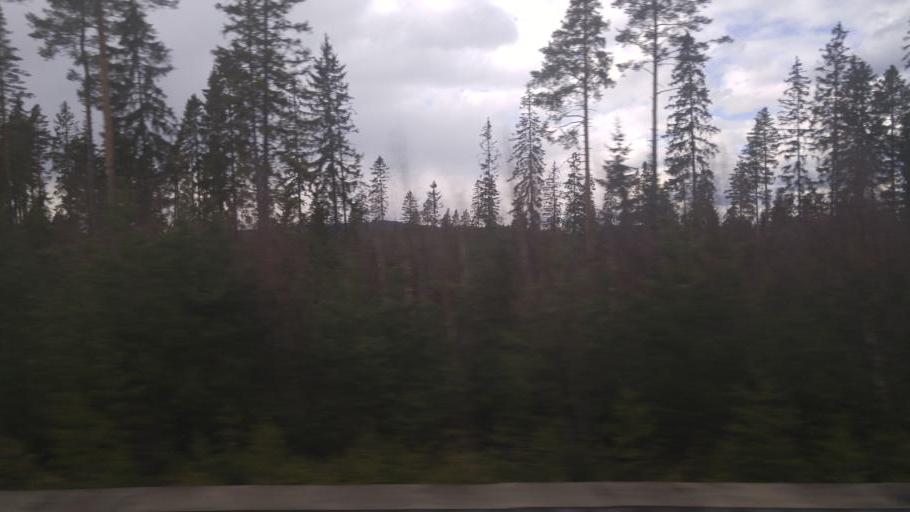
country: NO
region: Akershus
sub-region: Eidsvoll
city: Raholt
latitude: 60.2580
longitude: 11.1340
